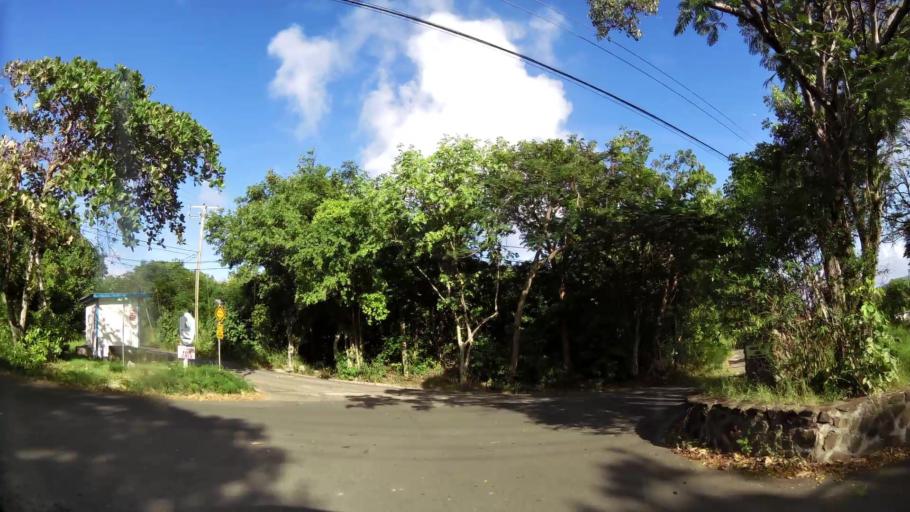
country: LC
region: Gros-Islet
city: Gros Islet
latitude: 14.1002
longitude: -60.9439
